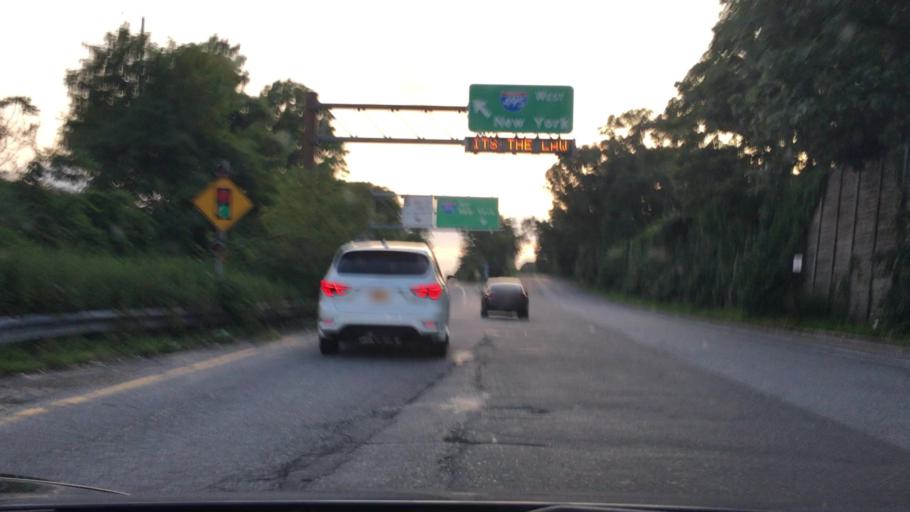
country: US
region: New York
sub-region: Suffolk County
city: Commack
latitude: 40.8054
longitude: -73.2952
